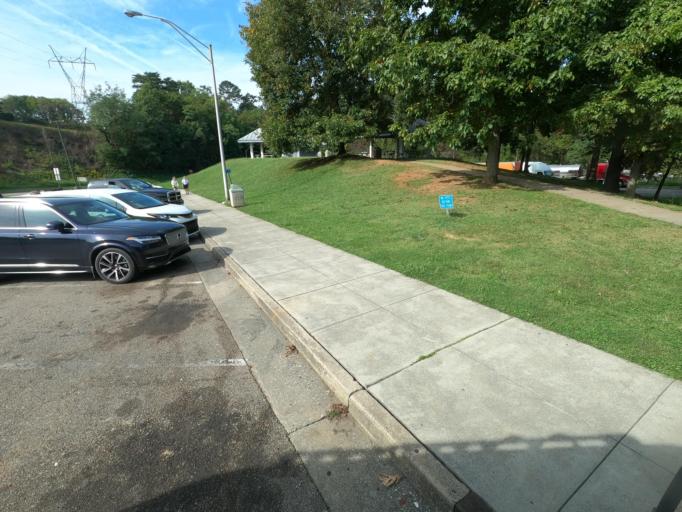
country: US
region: Tennessee
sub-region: Jefferson County
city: Dandridge
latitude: 36.0514
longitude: -83.4116
